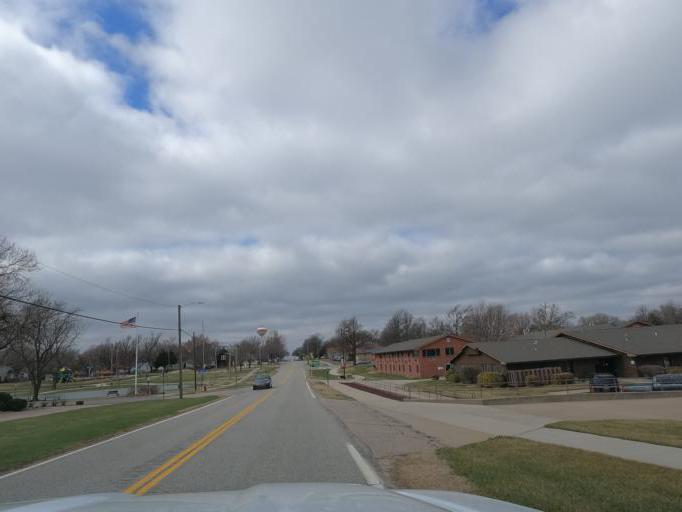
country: US
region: Kansas
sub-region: McPherson County
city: Inman
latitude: 38.2320
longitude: -97.7691
